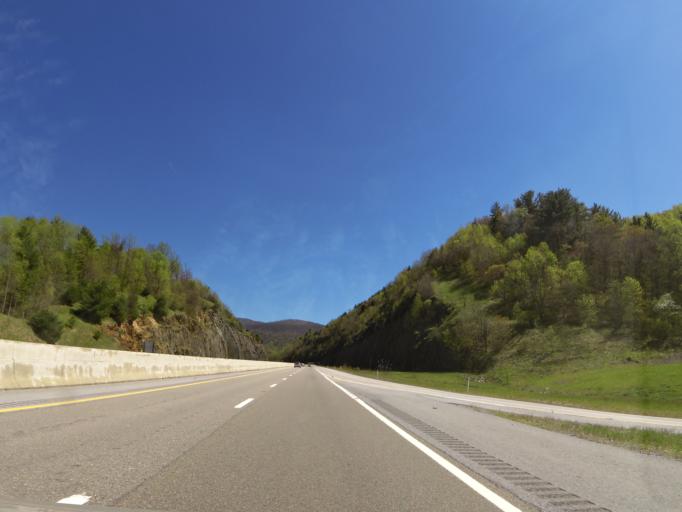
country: US
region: Tennessee
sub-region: Unicoi County
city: Banner Hill
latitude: 36.0101
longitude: -82.5456
